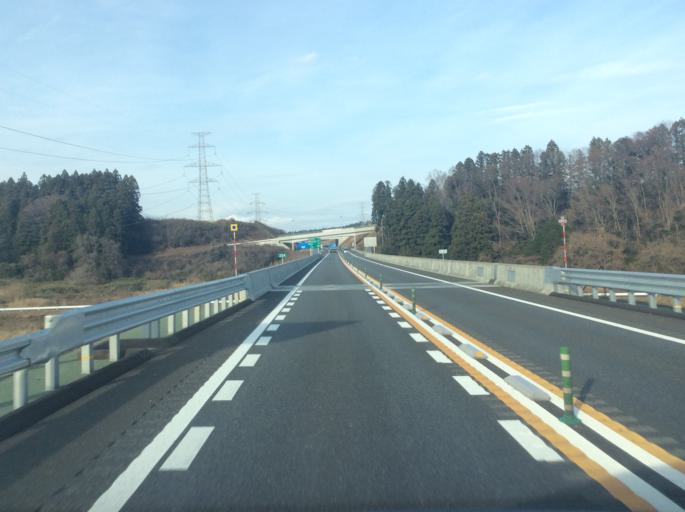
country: JP
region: Fukushima
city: Namie
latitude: 37.5086
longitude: 140.9428
